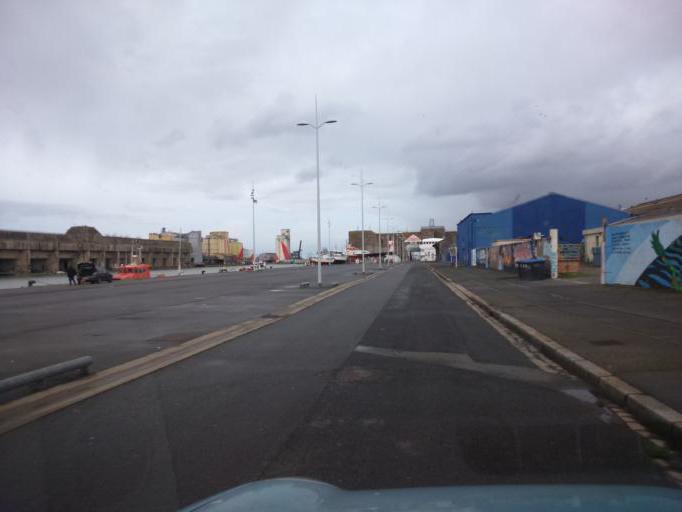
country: FR
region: Pays de la Loire
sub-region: Departement de la Loire-Atlantique
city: Saint-Nazaire
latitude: 47.2730
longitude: -2.2000
